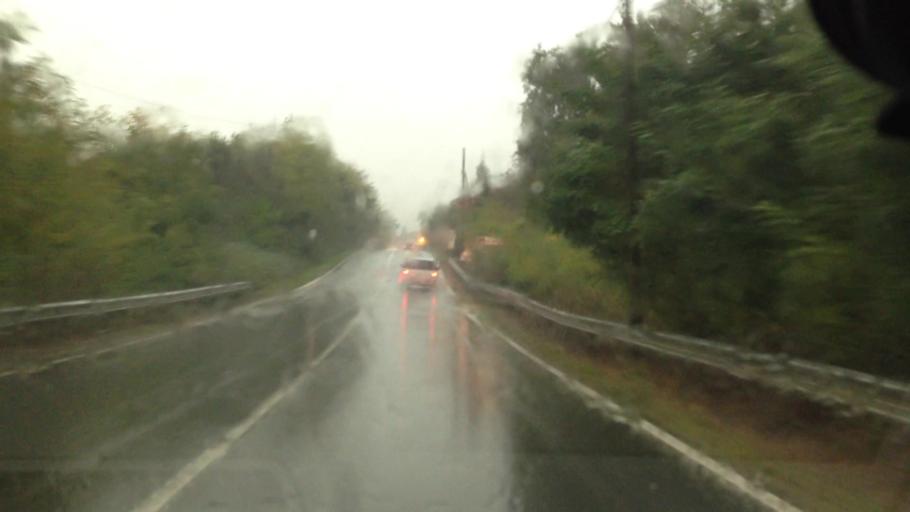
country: IT
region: Piedmont
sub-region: Provincia di Alessandria
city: Quattordio
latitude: 44.8992
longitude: 8.4167
